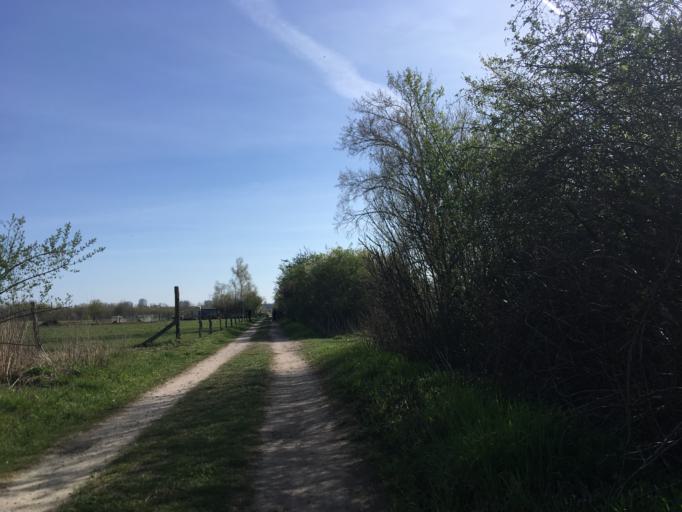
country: DE
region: Berlin
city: Wartenberg
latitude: 52.5908
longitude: 13.5106
